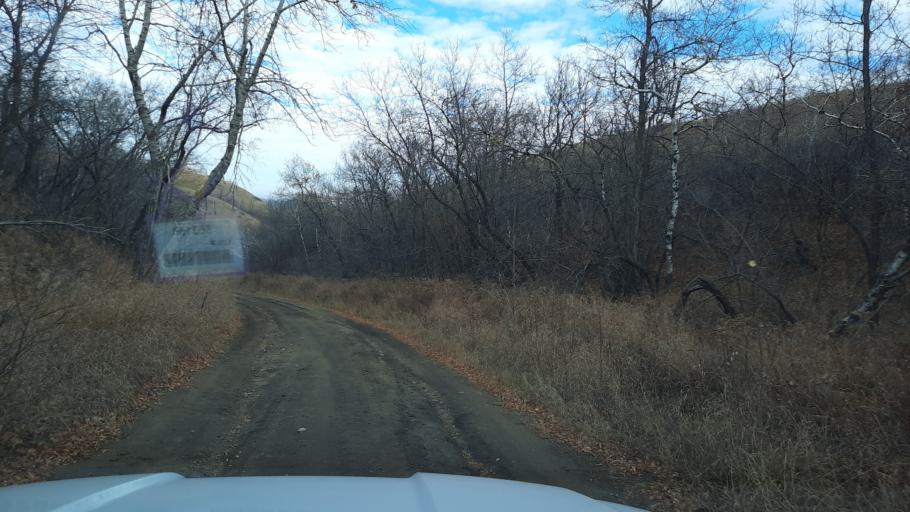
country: CA
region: Saskatchewan
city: Pilot Butte
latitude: 50.7777
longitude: -104.2107
